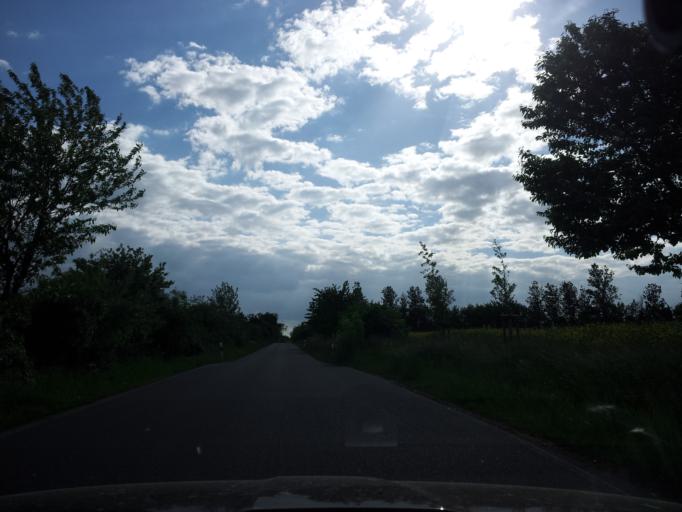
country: DE
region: Brandenburg
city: Niedergorsdorf
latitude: 51.9756
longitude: 12.9293
